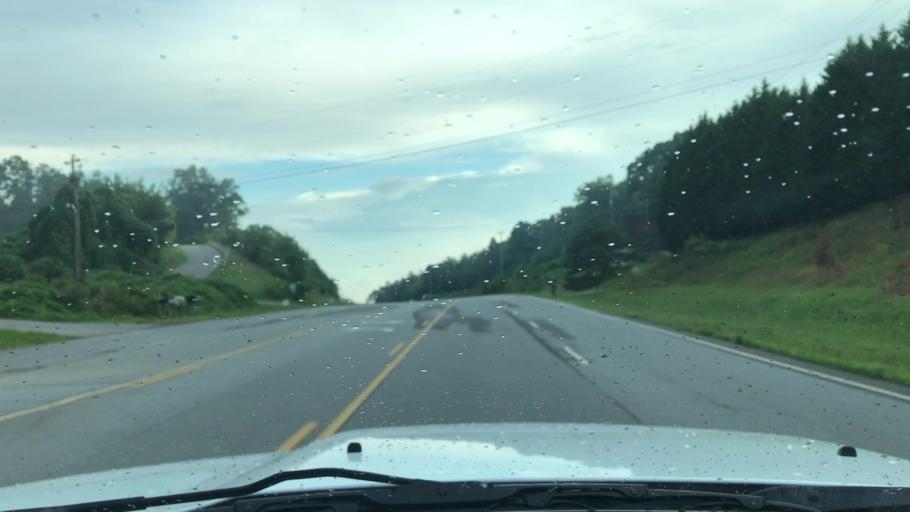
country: US
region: North Carolina
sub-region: Cherokee County
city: Murphy
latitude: 35.0107
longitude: -84.1272
